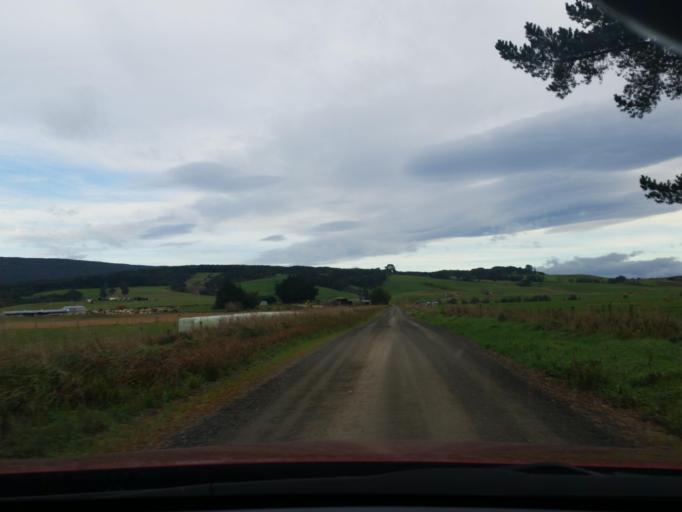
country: NZ
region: Southland
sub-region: Southland District
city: Riverton
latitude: -46.0997
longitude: 167.9477
